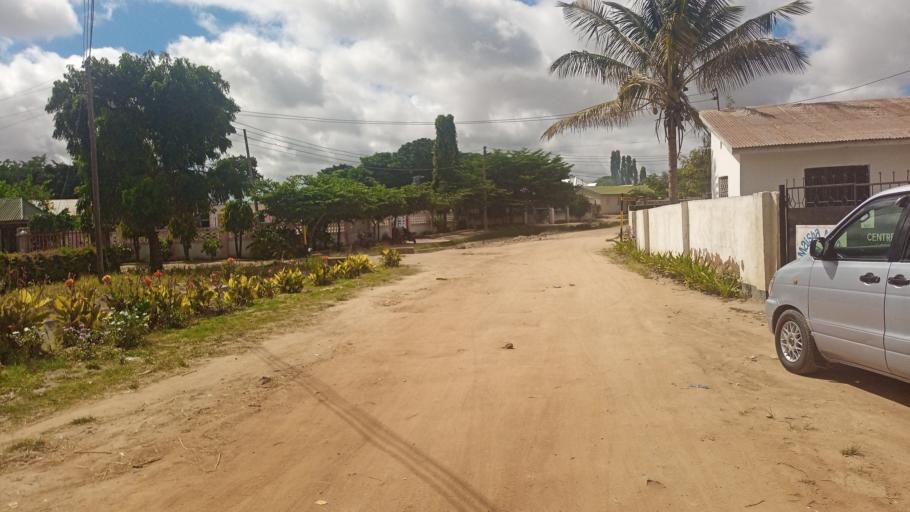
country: TZ
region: Dodoma
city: Dodoma
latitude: -6.1907
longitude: 35.7342
